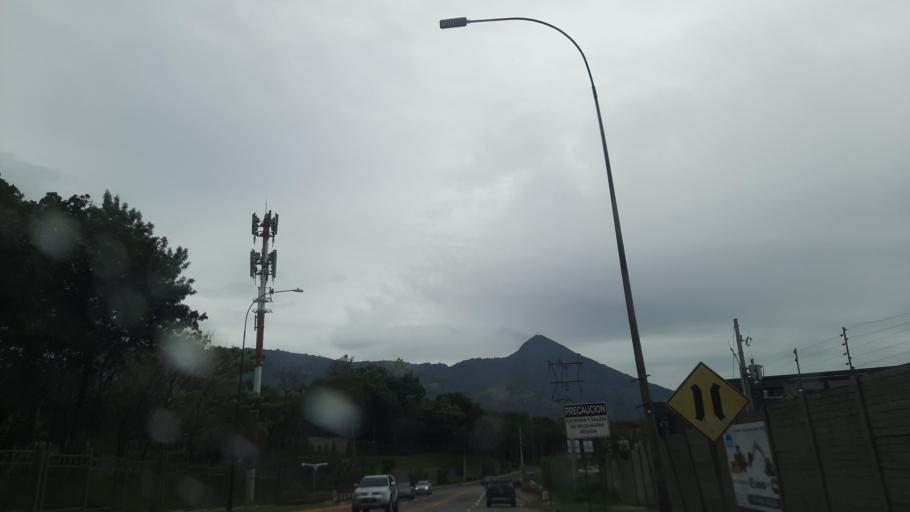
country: SV
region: La Libertad
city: Antiguo Cuscatlan
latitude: 13.6833
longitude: -89.2461
